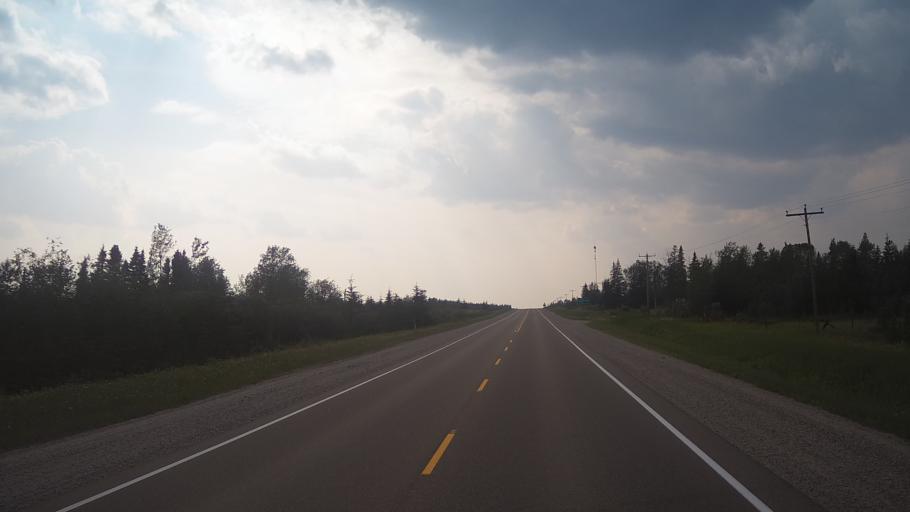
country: CA
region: Ontario
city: Kapuskasing
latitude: 49.5343
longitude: -82.9054
